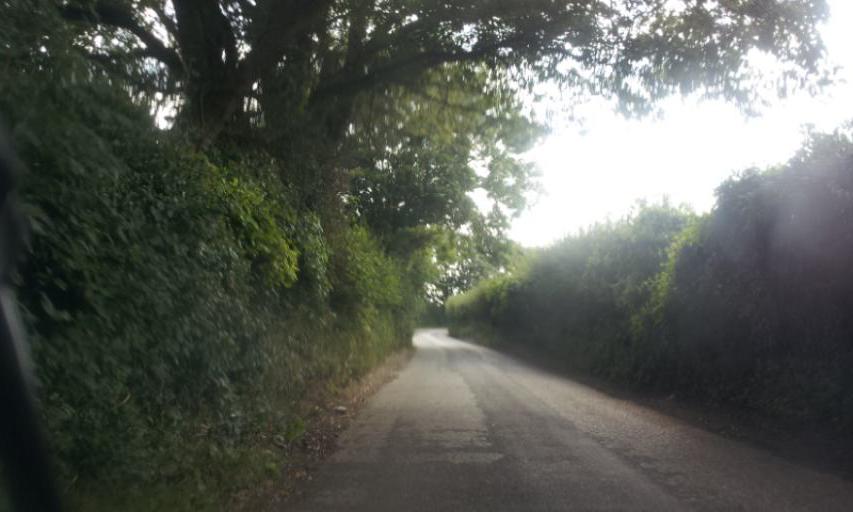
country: GB
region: England
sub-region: Kent
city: Maidstone
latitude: 51.2468
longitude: 0.5045
